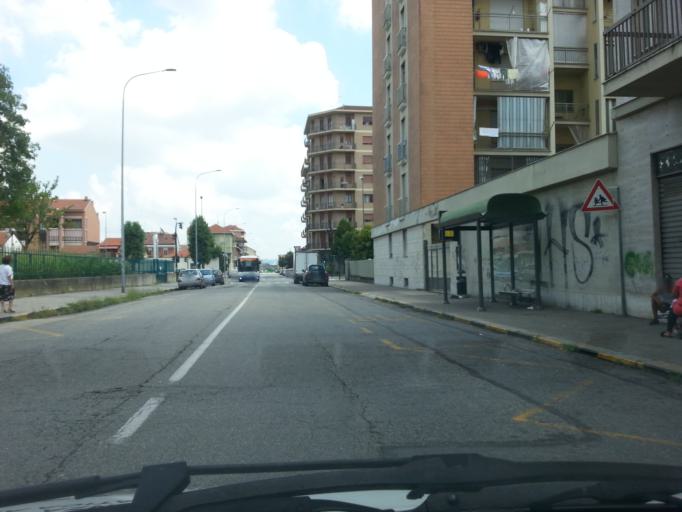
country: IT
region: Piedmont
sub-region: Provincia di Torino
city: Venaria Reale
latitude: 45.1084
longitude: 7.6624
